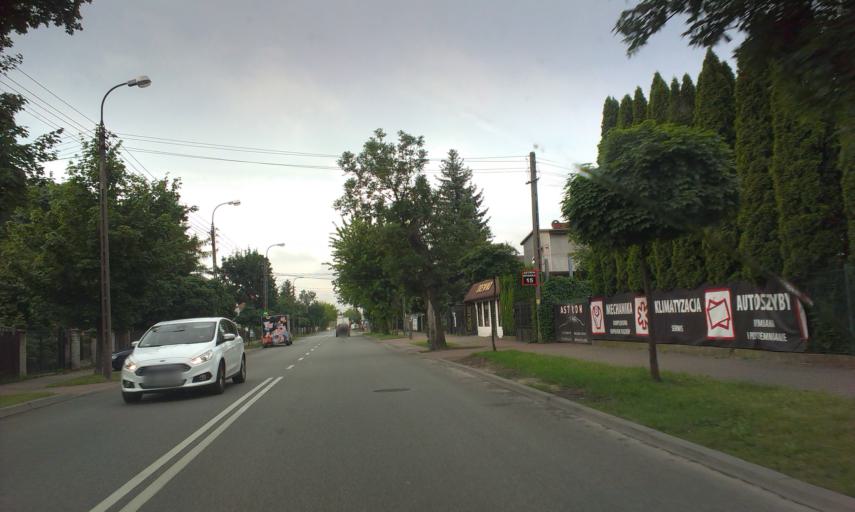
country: PL
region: Masovian Voivodeship
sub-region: Warszawa
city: Ursus
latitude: 52.1847
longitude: 20.8851
